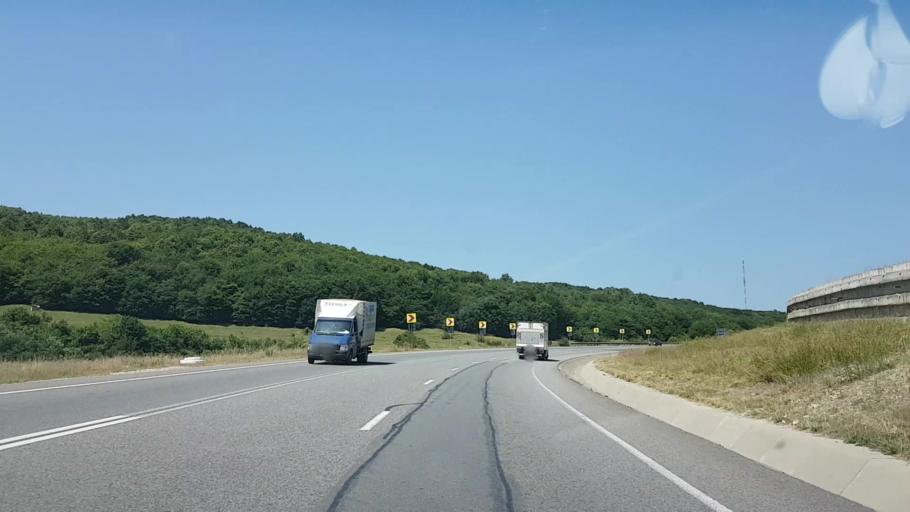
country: RO
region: Cluj
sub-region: Comuna Feleacu
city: Feleacu
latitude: 46.6945
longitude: 23.6360
